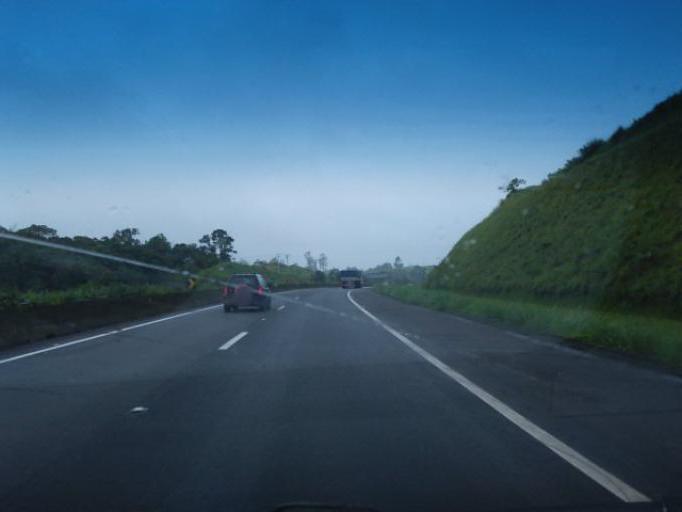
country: BR
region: Sao Paulo
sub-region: Cajati
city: Cajati
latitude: -24.7434
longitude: -48.1415
